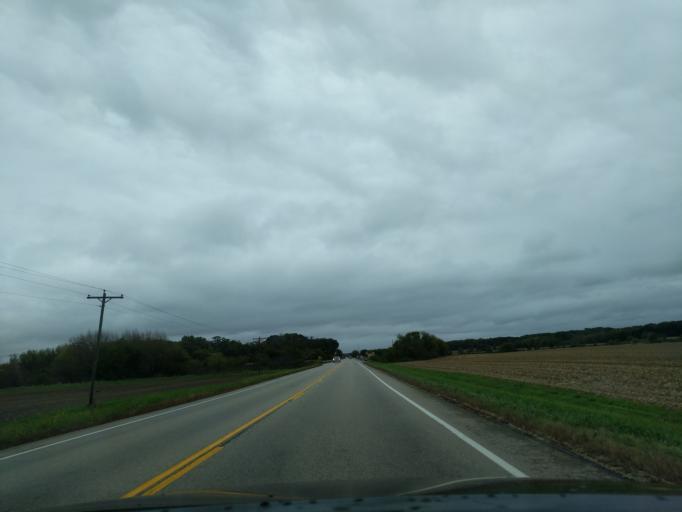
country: US
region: Illinois
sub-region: Ogle County
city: Oregon
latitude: 42.0034
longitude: -89.3694
